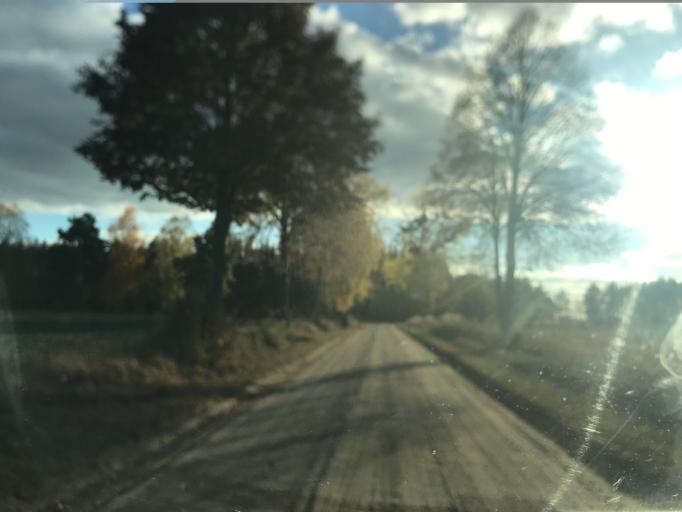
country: PL
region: Warmian-Masurian Voivodeship
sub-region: Powiat dzialdowski
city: Rybno
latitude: 53.3733
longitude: 19.8307
